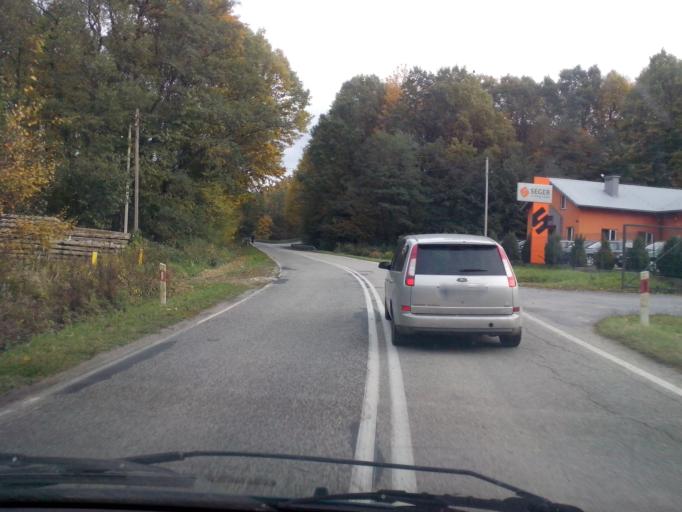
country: PL
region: Subcarpathian Voivodeship
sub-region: Powiat strzyzowski
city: Wisniowa
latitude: 49.8777
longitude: 21.6463
